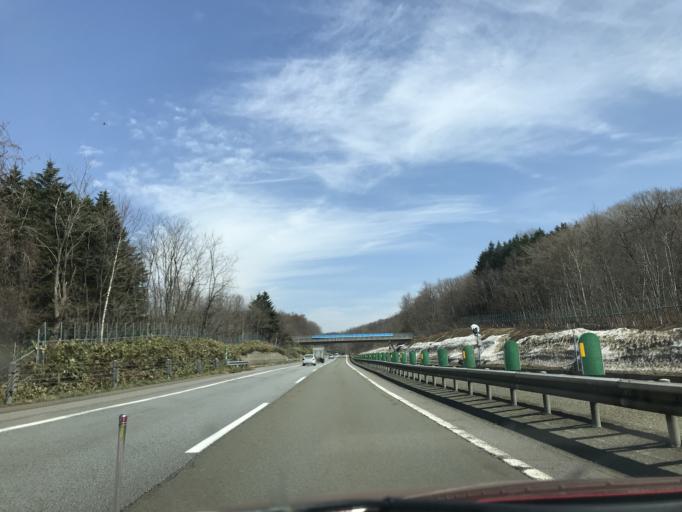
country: JP
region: Hokkaido
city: Bibai
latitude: 43.2820
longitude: 141.8554
